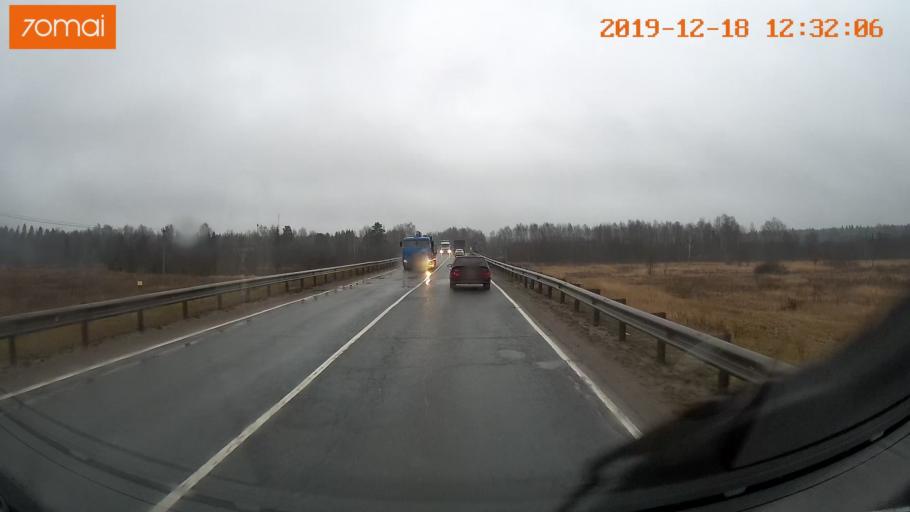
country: RU
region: Moskovskaya
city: Rumyantsevo
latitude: 56.1040
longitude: 36.5476
